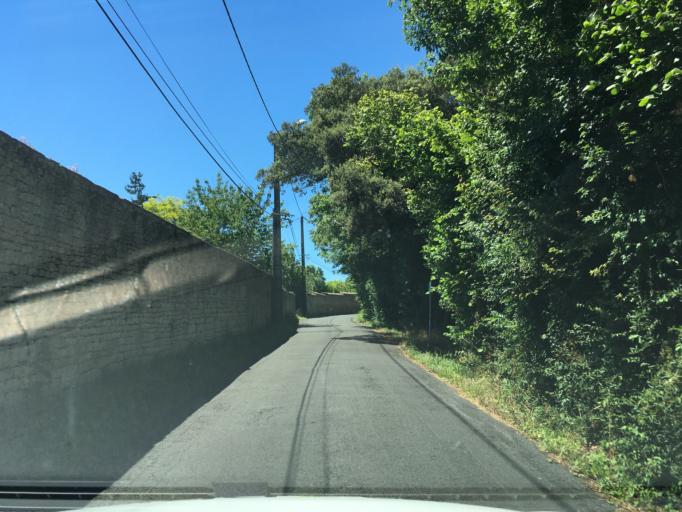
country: FR
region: Poitou-Charentes
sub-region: Departement des Deux-Sevres
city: Niort
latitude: 46.3316
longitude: -0.4417
